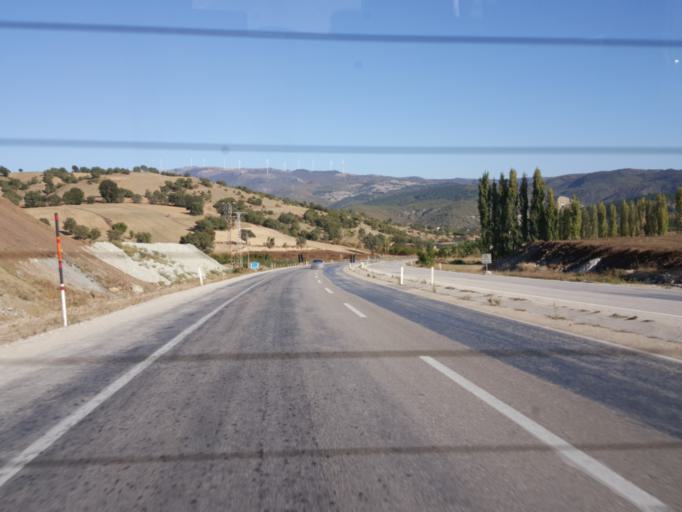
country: TR
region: Amasya
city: Ezinepazari
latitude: 40.5570
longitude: 36.1382
